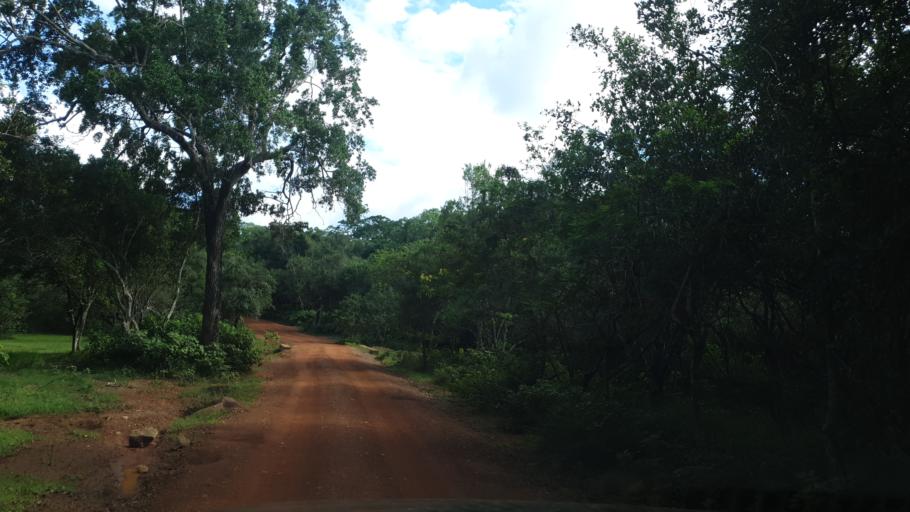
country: LK
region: North Central
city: Anuradhapura
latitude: 8.3834
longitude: 80.0616
